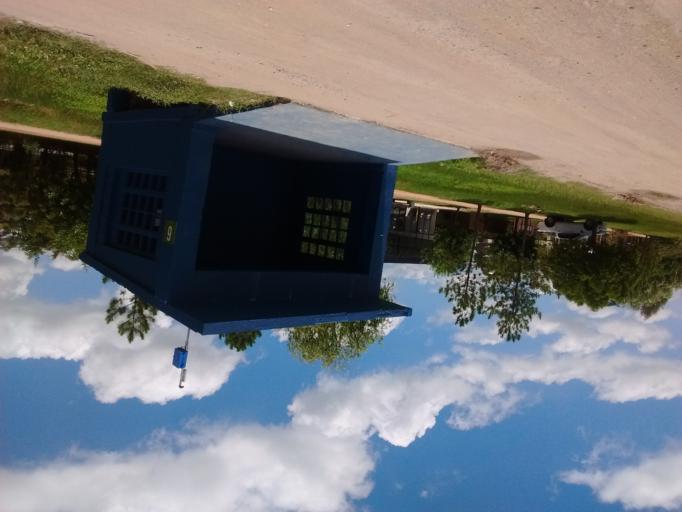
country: AR
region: Santa Fe
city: Funes
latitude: -32.9234
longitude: -60.7934
